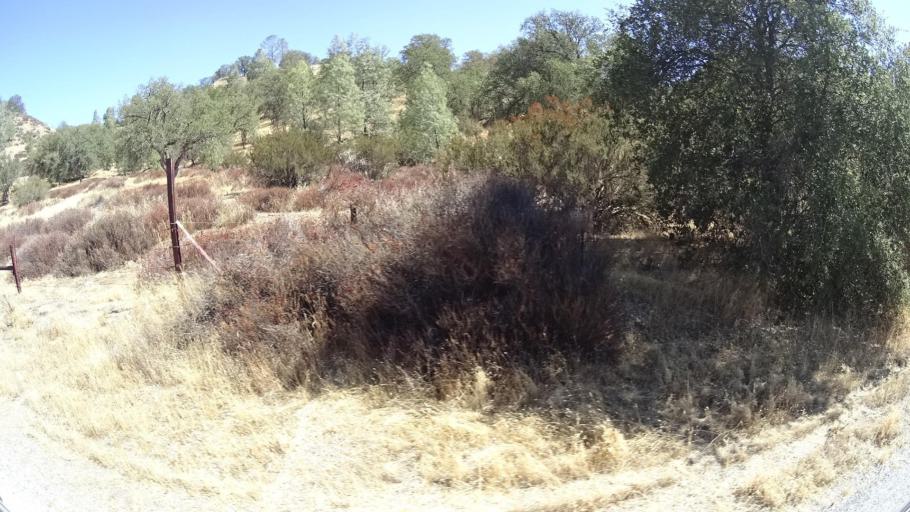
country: US
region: California
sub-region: San Luis Obispo County
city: San Miguel
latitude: 35.8875
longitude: -120.5590
